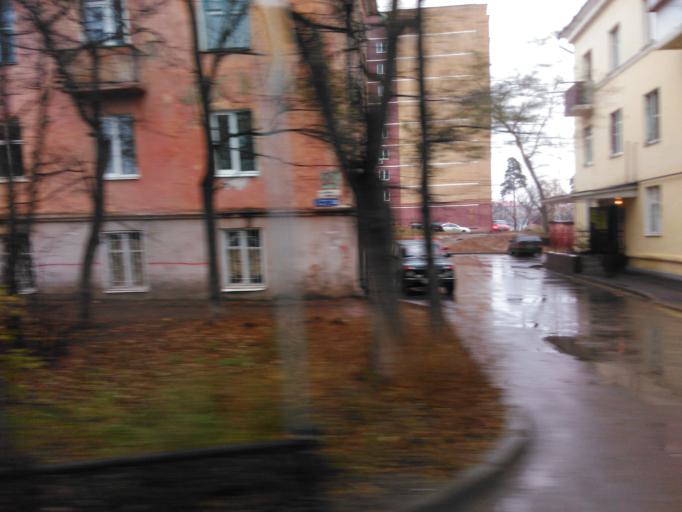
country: RU
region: Tatarstan
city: Osinovo
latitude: 55.8215
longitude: 48.8985
